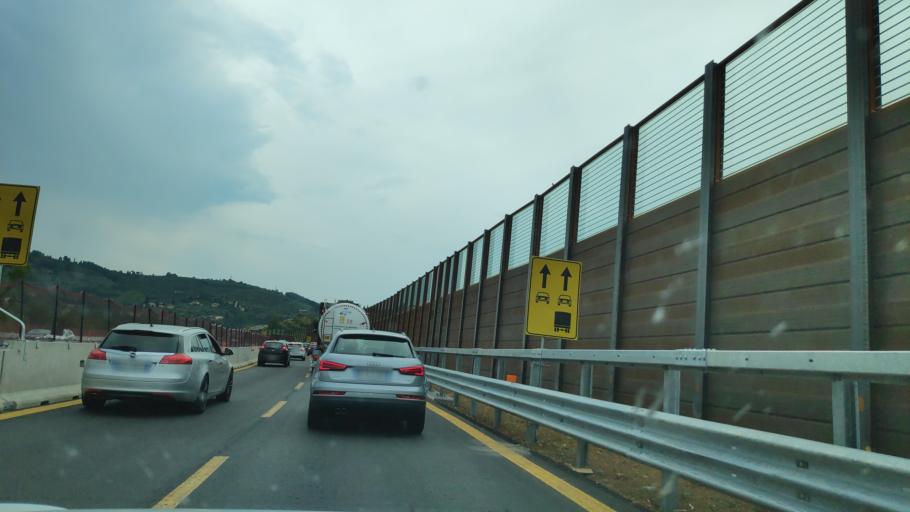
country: IT
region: Tuscany
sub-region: Province of Florence
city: Grassina Ponte a Ema
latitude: 43.7330
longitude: 11.3089
